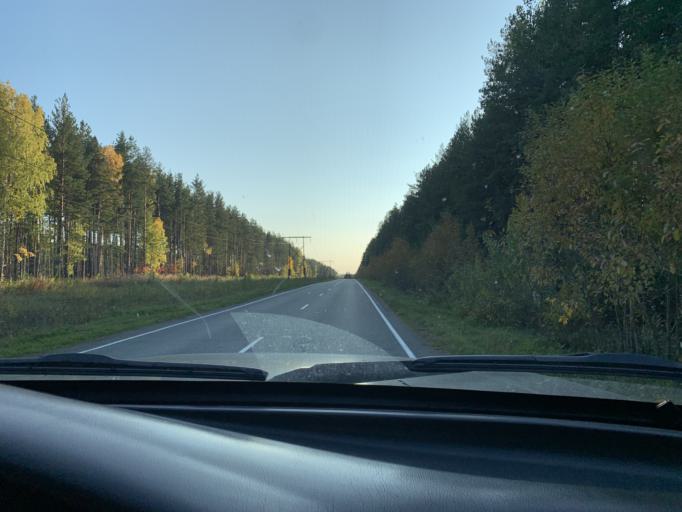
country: RU
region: Sverdlovsk
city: Verkhneye Dubrovo
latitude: 56.8685
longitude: 61.0966
